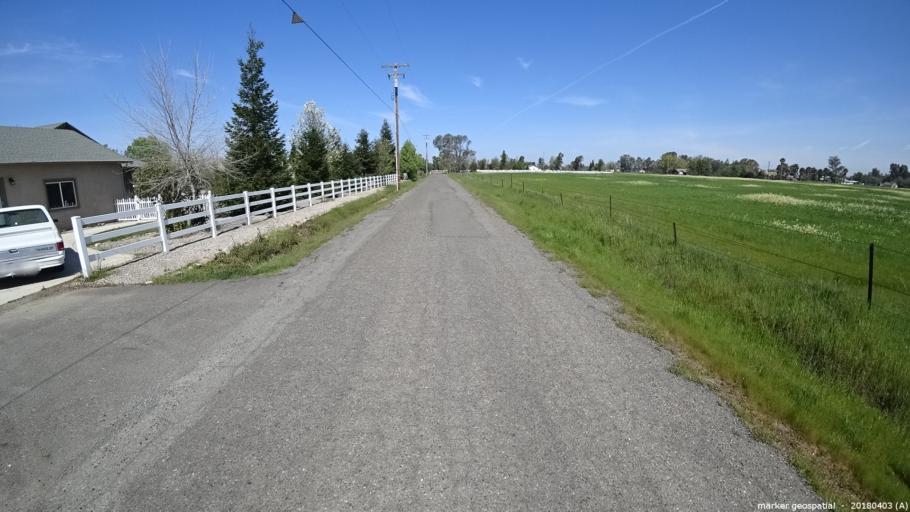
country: US
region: California
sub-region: Sacramento County
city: Wilton
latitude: 38.4004
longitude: -121.2690
